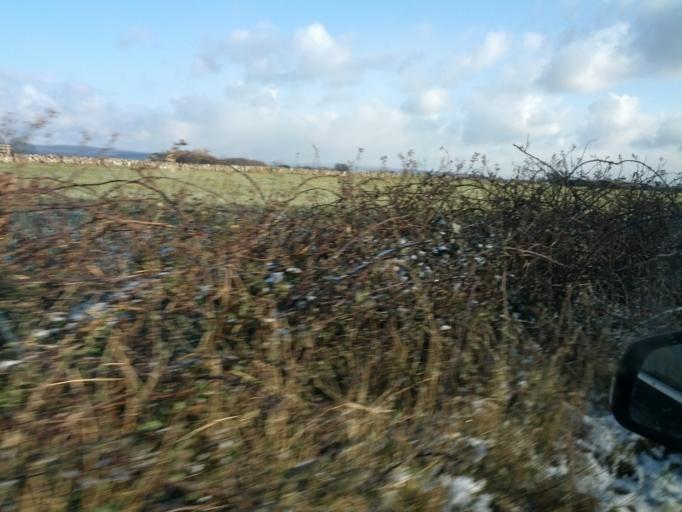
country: IE
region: Connaught
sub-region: County Galway
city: Gort
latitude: 53.1709
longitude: -8.7974
